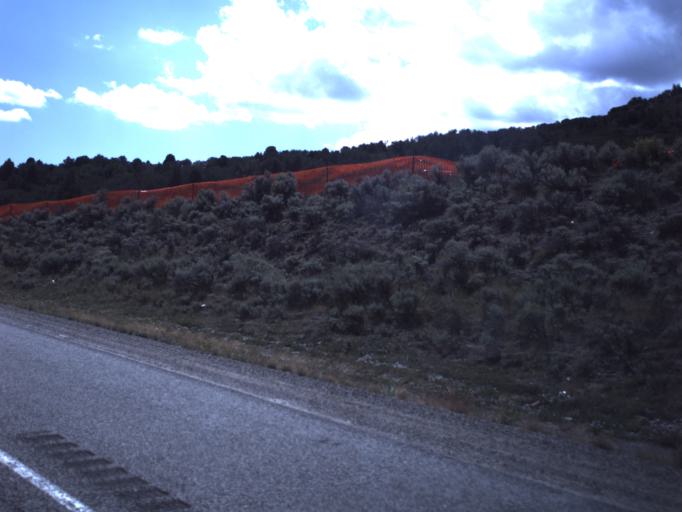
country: US
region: Utah
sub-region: Wayne County
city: Loa
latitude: 38.7801
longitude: -111.4852
